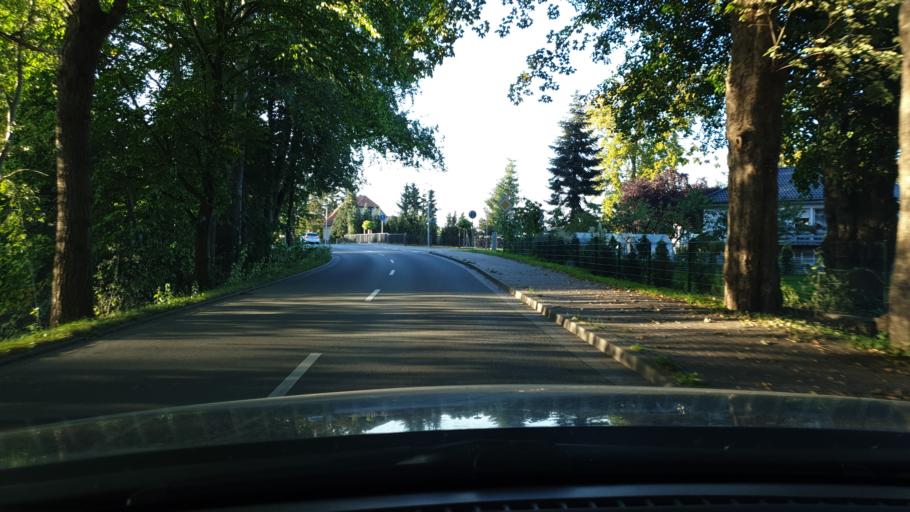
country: DE
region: Mecklenburg-Vorpommern
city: Wittenburg
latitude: 53.4884
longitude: 11.0205
